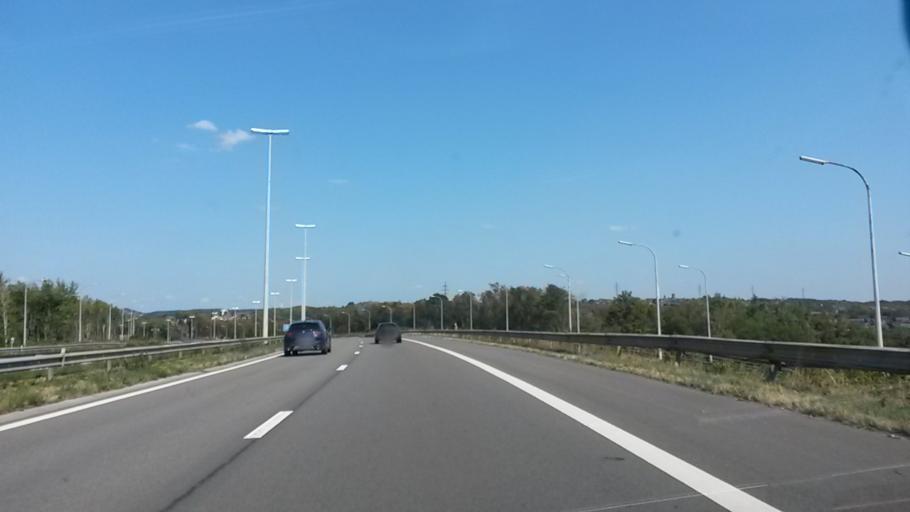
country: BE
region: Wallonia
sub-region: Province du Hainaut
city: Chatelet
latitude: 50.4134
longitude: 4.4987
